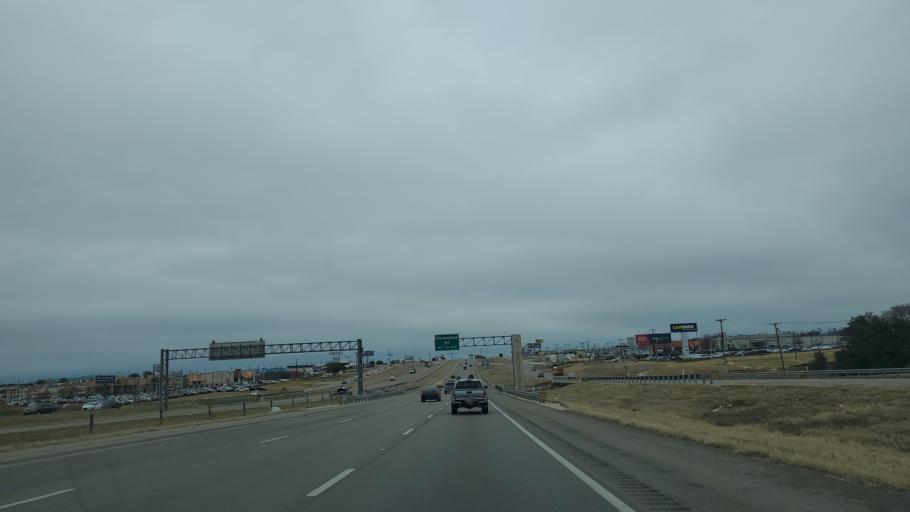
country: US
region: Texas
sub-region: Bell County
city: Killeen
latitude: 31.0852
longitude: -97.7087
